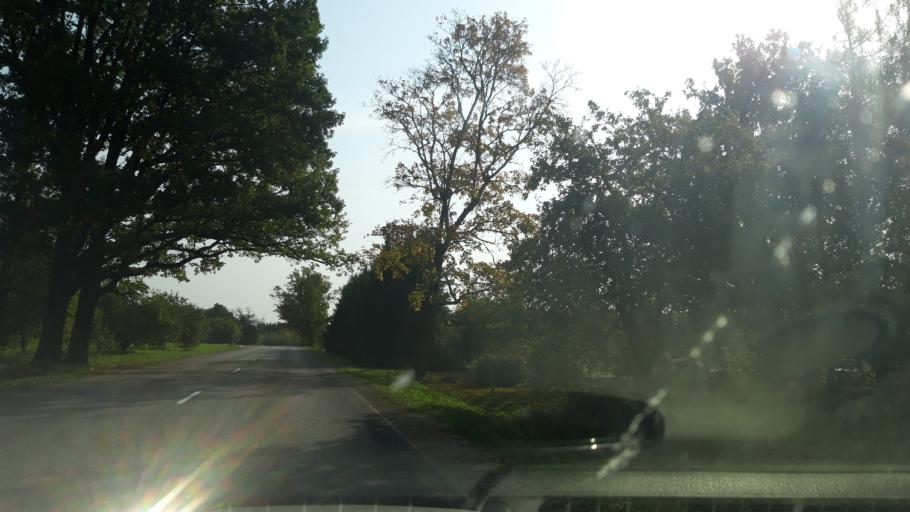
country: LV
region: Koceni
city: Koceni
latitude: 57.6267
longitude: 25.2680
